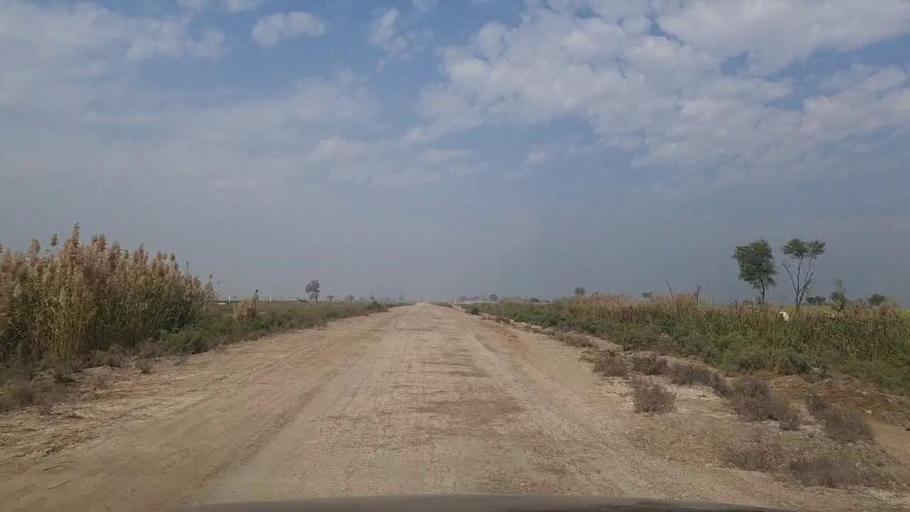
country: PK
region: Sindh
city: Daur
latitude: 26.3883
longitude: 68.3513
